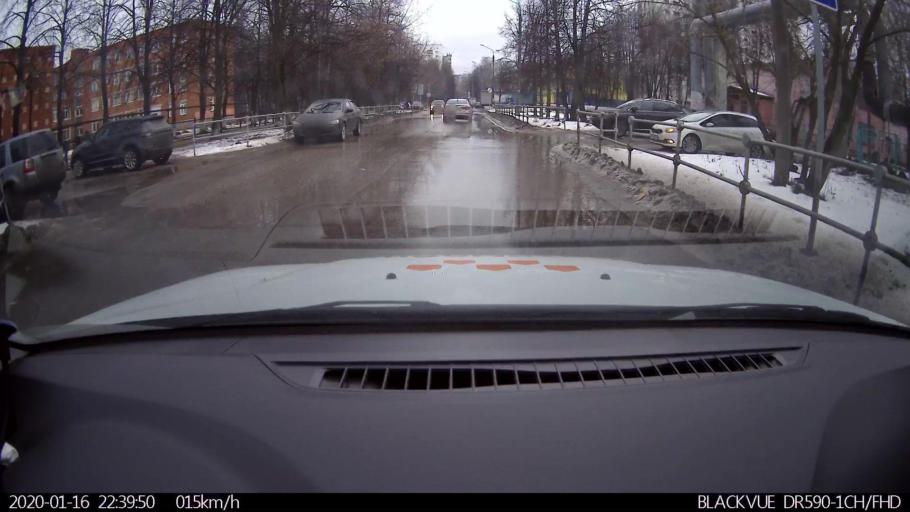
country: RU
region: Nizjnij Novgorod
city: Nizhniy Novgorod
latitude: 56.2780
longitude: 43.9149
